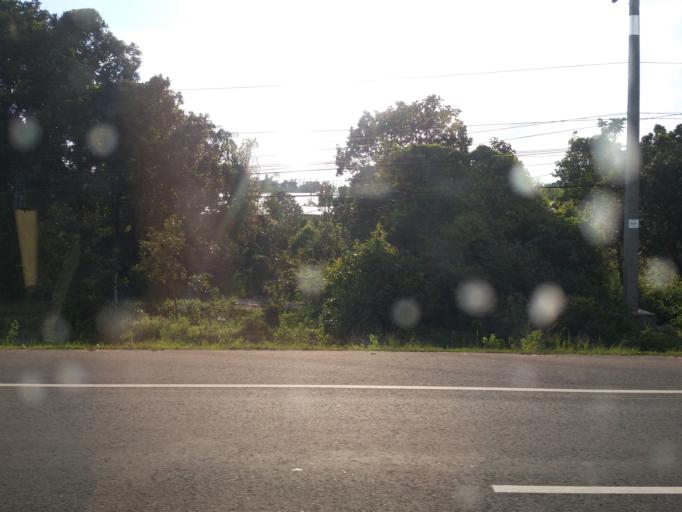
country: TH
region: Changwat Ubon Ratchathani
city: Sirindhorn
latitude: 15.1965
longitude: 105.3691
